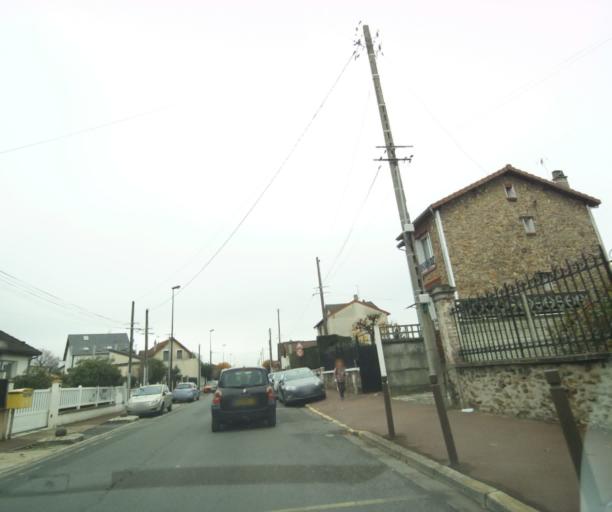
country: FR
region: Ile-de-France
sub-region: Departement de Seine-Saint-Denis
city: Le Raincy
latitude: 48.9174
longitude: 2.5228
